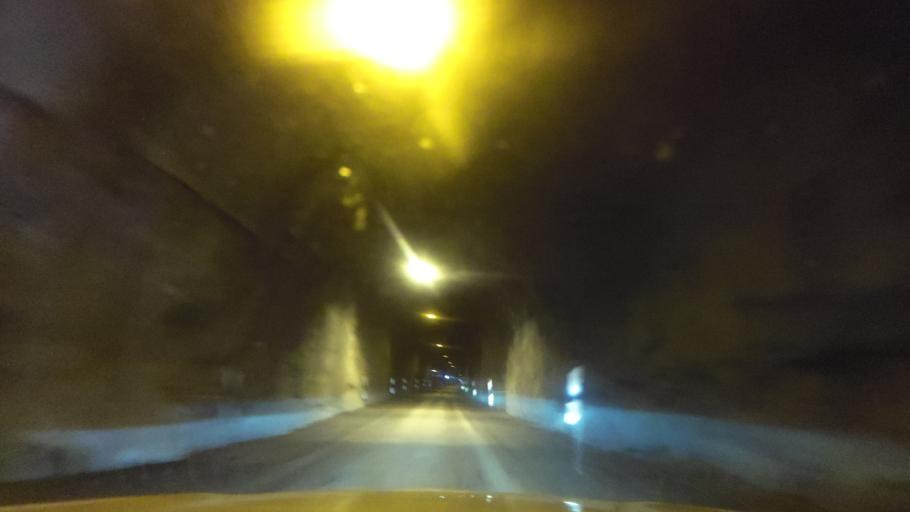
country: IS
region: Westfjords
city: Isafjoerdur
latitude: 66.0300
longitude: -23.3414
